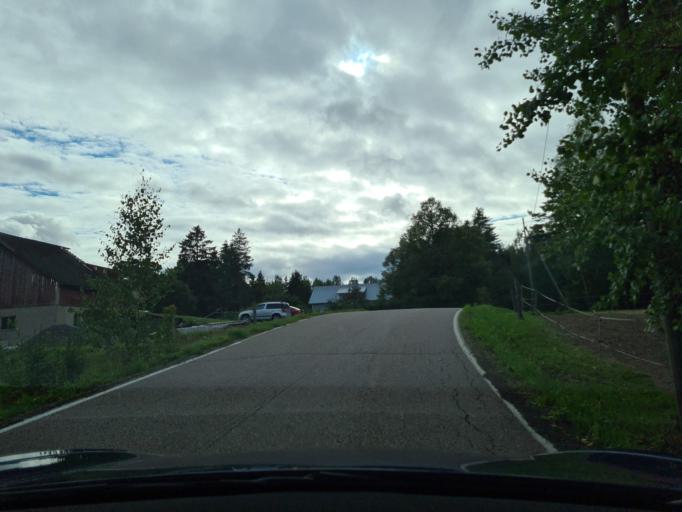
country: FI
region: Uusimaa
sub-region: Helsinki
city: Vihti
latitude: 60.4725
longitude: 24.4584
